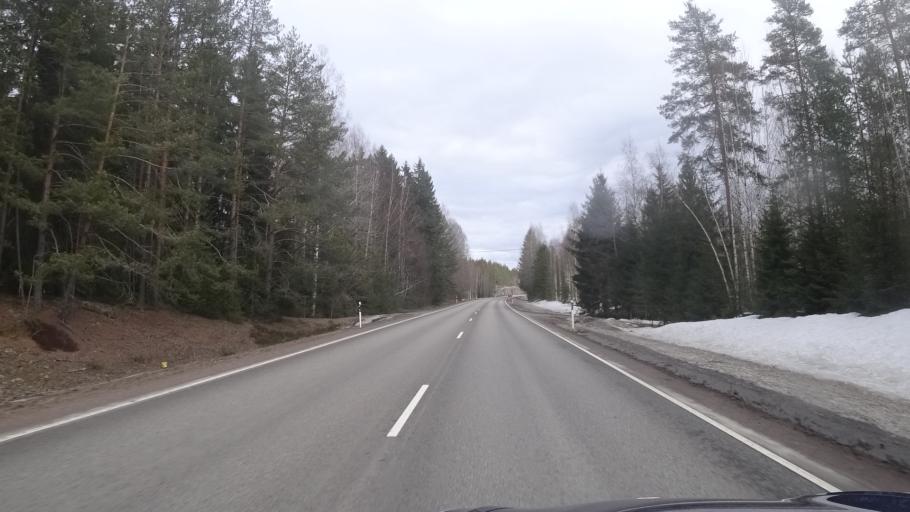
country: FI
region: Kymenlaakso
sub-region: Kouvola
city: Anjala
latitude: 60.6926
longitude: 26.7127
